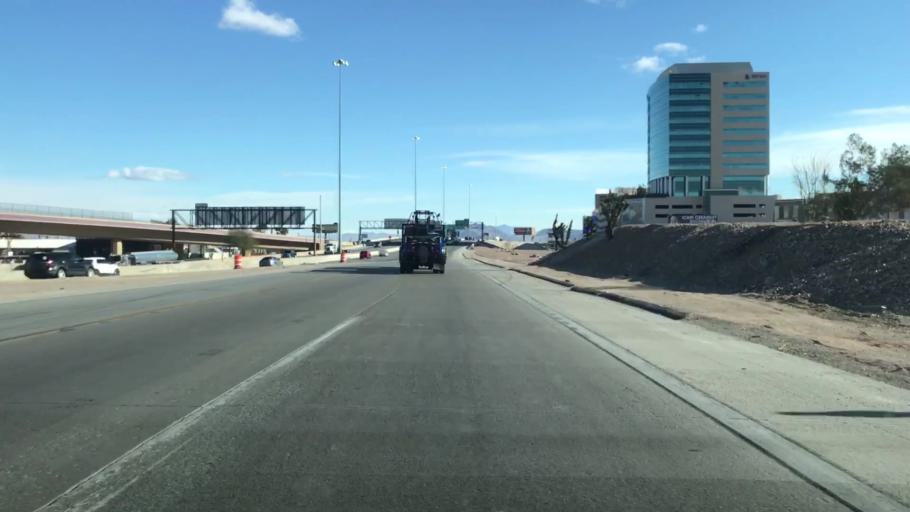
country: US
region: Nevada
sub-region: Clark County
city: Las Vegas
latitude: 36.1737
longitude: -115.1527
